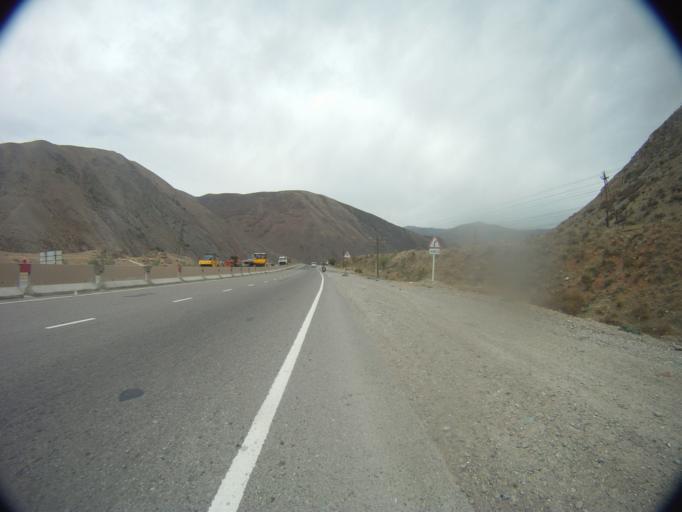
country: KG
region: Chuy
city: Bystrovka
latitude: 42.6821
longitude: 75.8905
